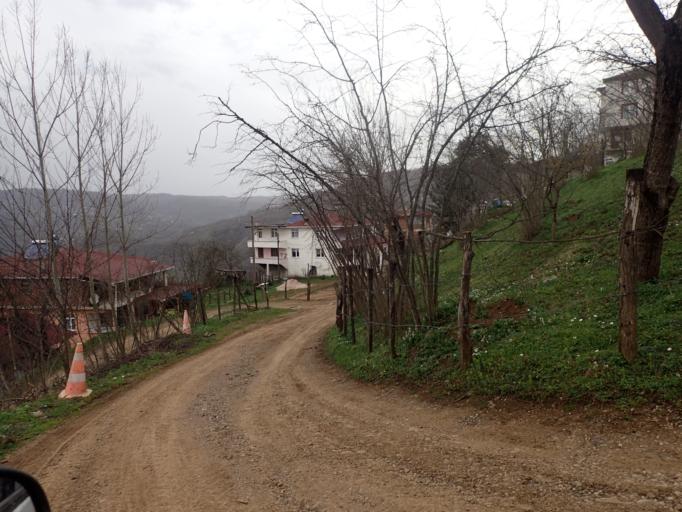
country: TR
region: Ordu
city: Camas
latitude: 40.8920
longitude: 37.4962
